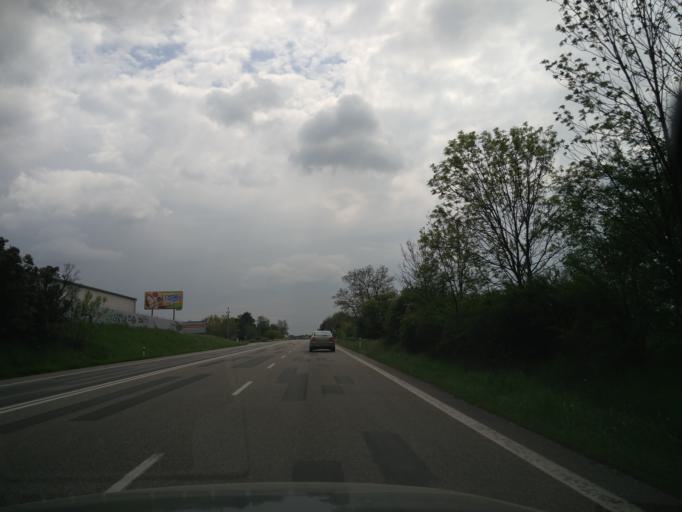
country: CZ
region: Jihocesky
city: Kamenny Ujezd
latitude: 48.9013
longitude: 14.4400
